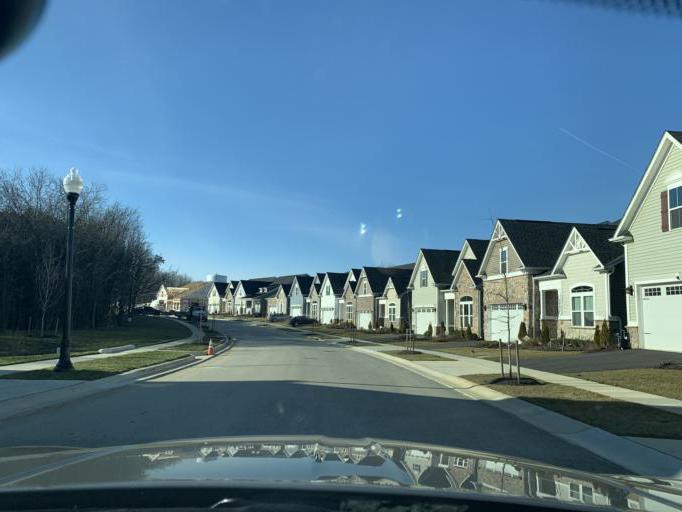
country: US
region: Maryland
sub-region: Anne Arundel County
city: Crofton
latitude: 39.0287
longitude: -76.7313
